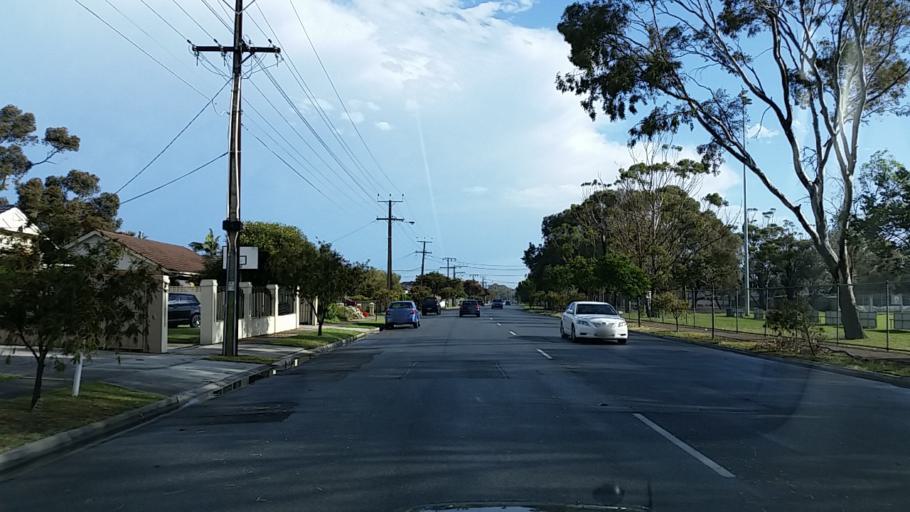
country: AU
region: South Australia
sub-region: Charles Sturt
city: Henley Beach
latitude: -34.9190
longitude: 138.5014
